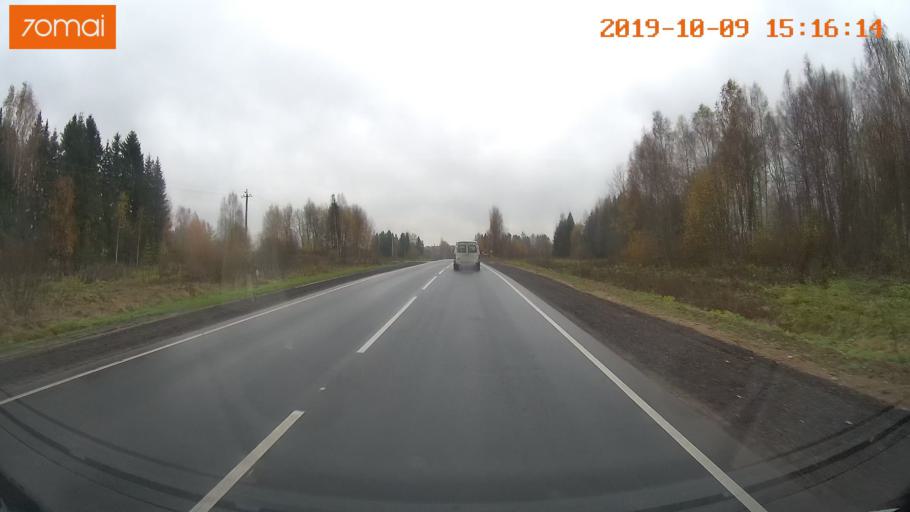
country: RU
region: Kostroma
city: Susanino
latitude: 58.1122
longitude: 41.5865
